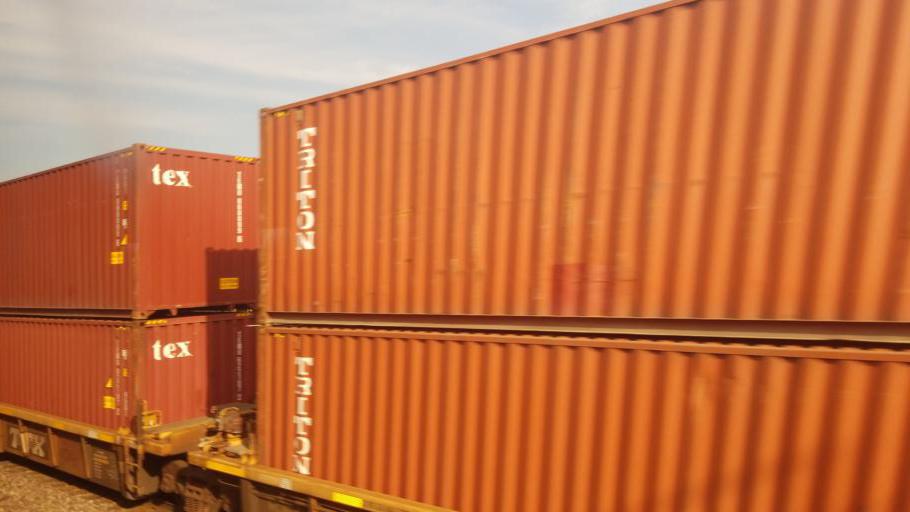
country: US
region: Illinois
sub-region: Kane County
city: Aurora
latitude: 41.7728
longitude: -88.2578
